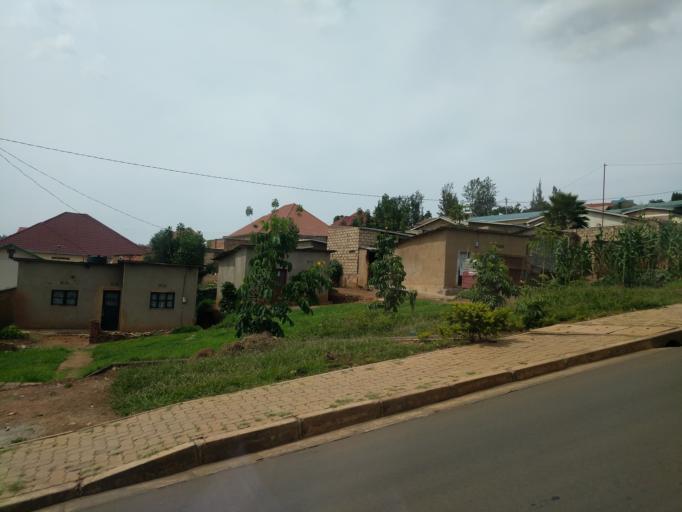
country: RW
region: Kigali
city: Kigali
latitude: -1.9740
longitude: 30.1206
